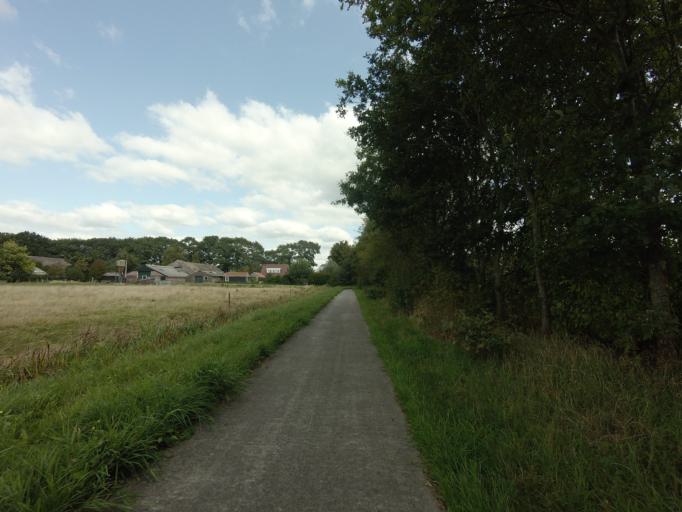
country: NL
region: Drenthe
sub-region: Gemeente De Wolden
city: Ruinen
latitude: 52.7012
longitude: 6.3043
